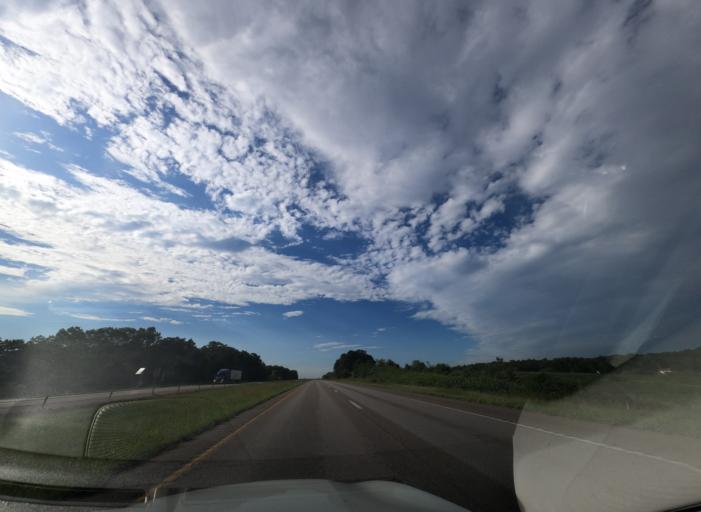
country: US
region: Missouri
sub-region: Jefferson County
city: Crystal City
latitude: 38.0454
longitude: -90.2663
